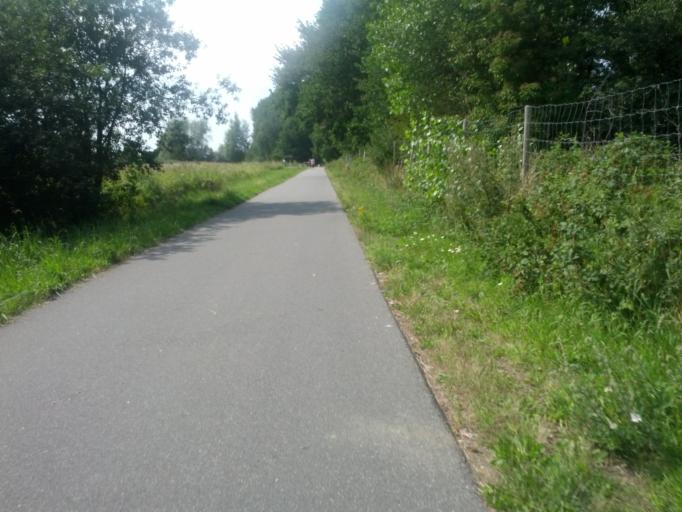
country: DE
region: Mecklenburg-Vorpommern
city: Bastorf
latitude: 54.1519
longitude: 11.6999
